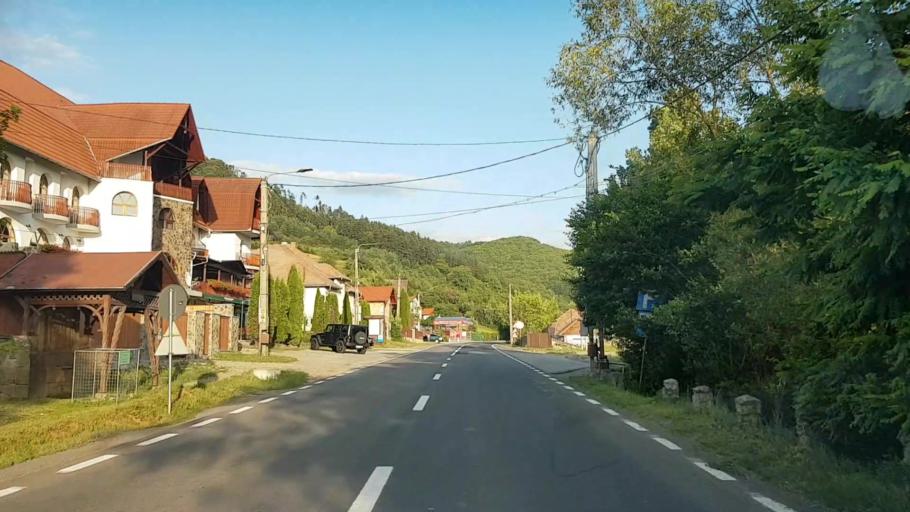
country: RO
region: Harghita
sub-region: Comuna Corund
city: Corund
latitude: 46.4685
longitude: 25.2001
